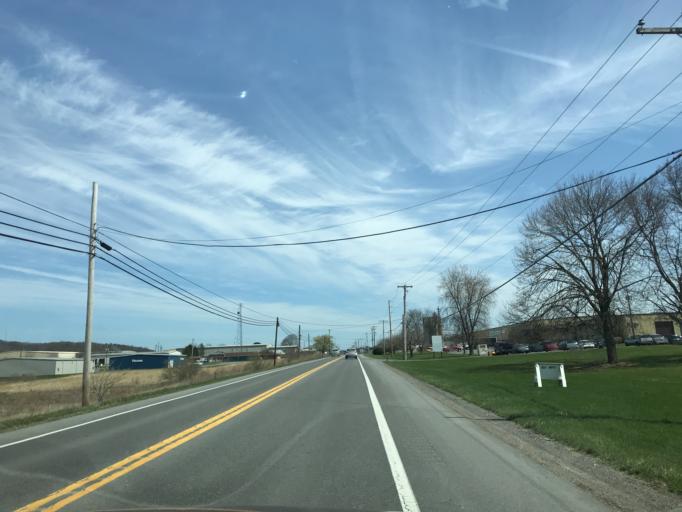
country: US
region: Pennsylvania
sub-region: Snyder County
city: Selinsgrove
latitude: 40.8059
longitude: -76.9166
